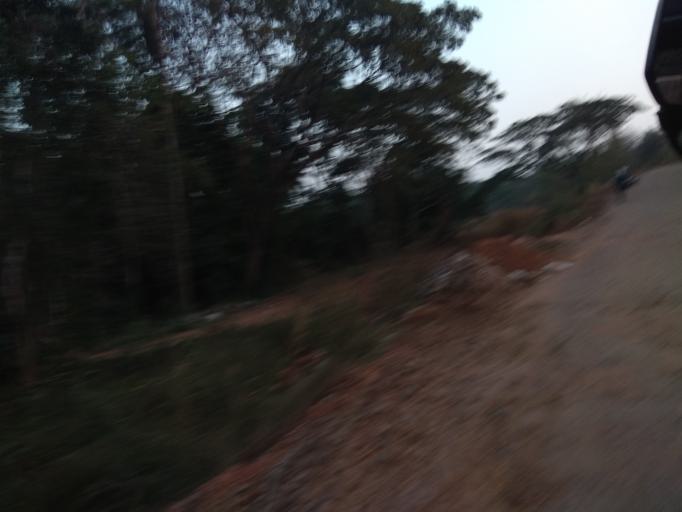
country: IN
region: Karnataka
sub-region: Dakshina Kannada
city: Mangalore
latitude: 12.9295
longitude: 74.8773
